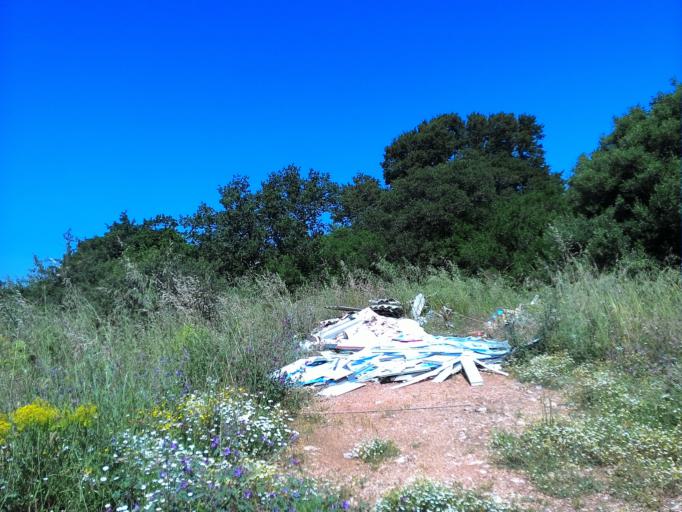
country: IT
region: Apulia
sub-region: Provincia di Bari
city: Noci
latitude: 40.8181
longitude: 17.1360
